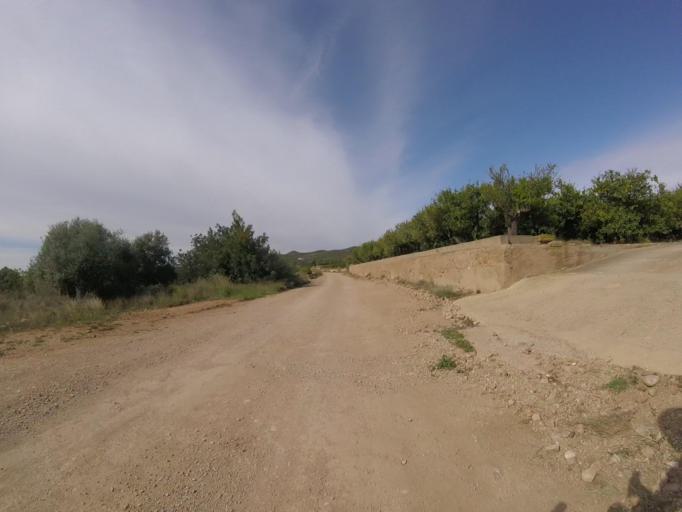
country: ES
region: Valencia
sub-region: Provincia de Castello
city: Torreblanca
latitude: 40.1989
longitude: 0.1645
